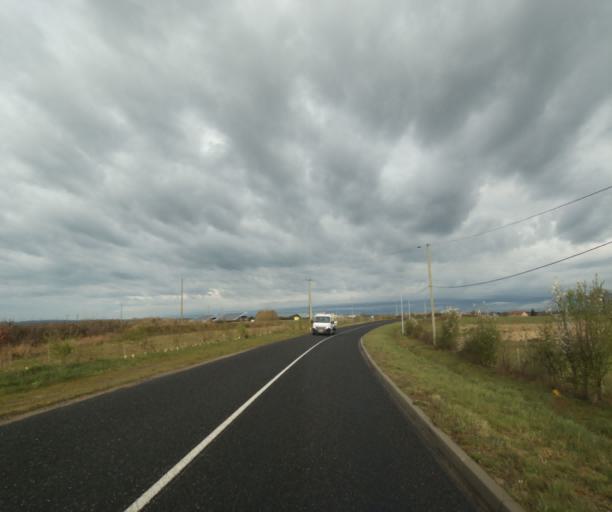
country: FR
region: Auvergne
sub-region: Departement de l'Allier
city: Toulon-sur-Allier
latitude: 46.5342
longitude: 3.3882
